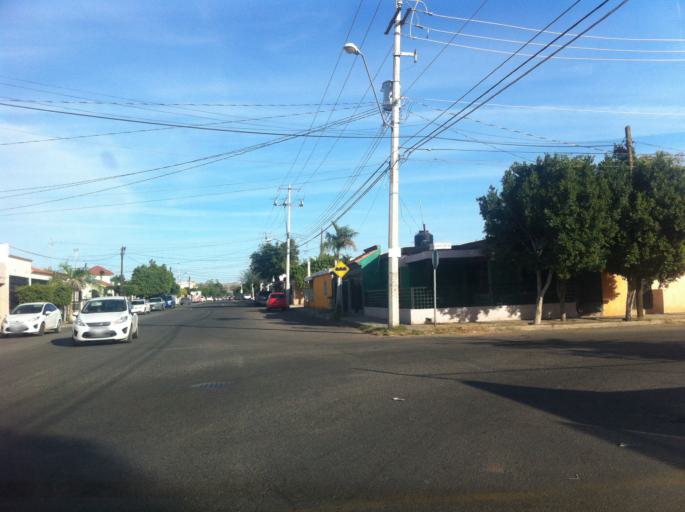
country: MX
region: Sonora
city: Hermosillo
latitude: 29.1003
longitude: -110.9903
